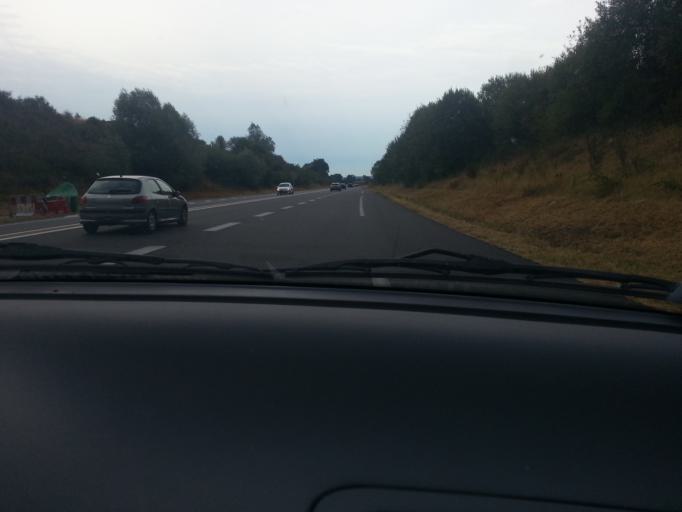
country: FR
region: Auvergne
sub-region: Departement de l'Allier
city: Molinet
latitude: 46.4560
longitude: 3.9179
